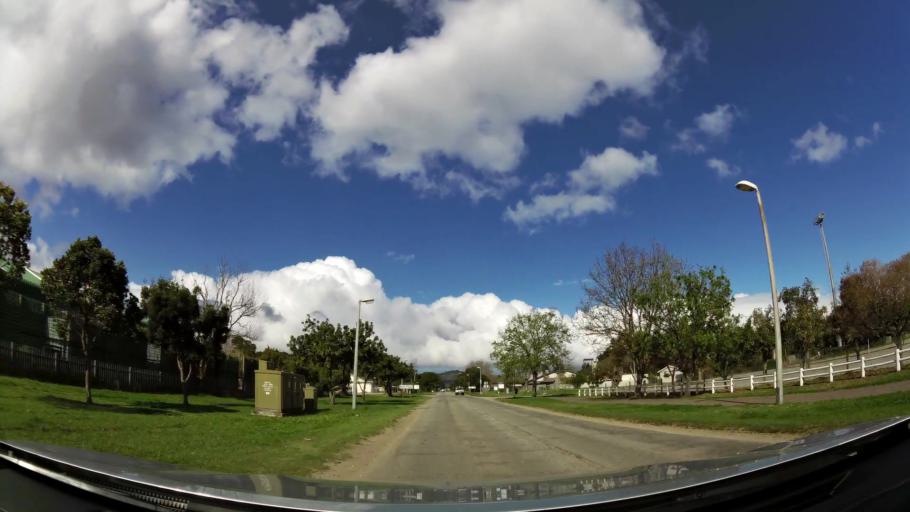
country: ZA
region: Western Cape
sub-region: Eden District Municipality
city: Knysna
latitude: -34.0484
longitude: 23.0701
